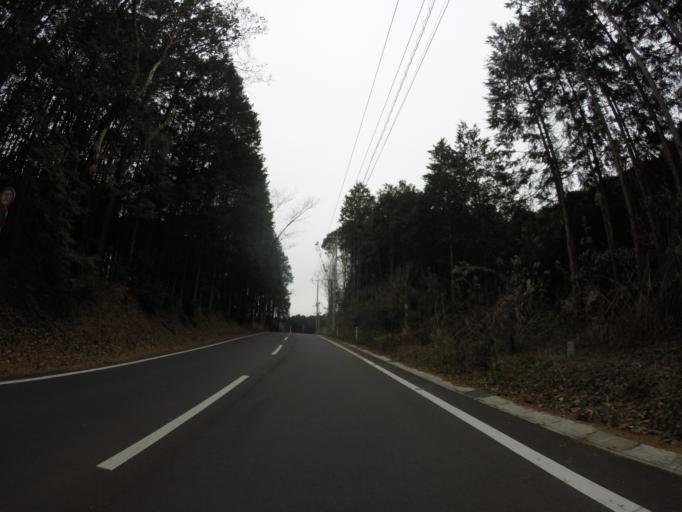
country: JP
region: Shizuoka
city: Fujinomiya
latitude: 35.2339
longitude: 138.5820
